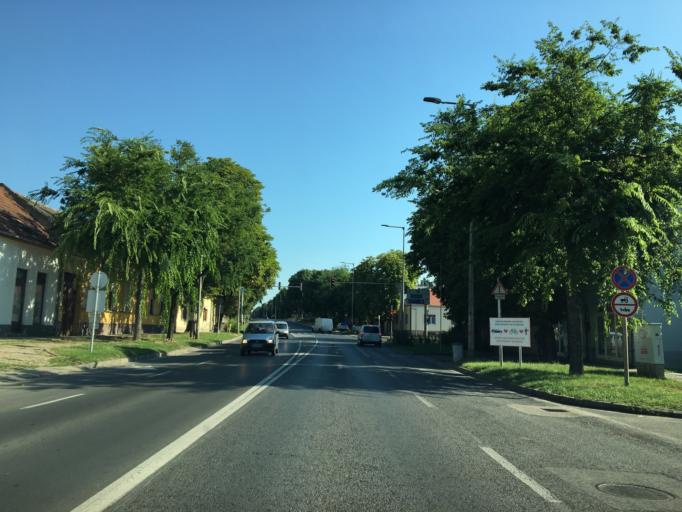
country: HU
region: Tolna
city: Szekszard
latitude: 46.3552
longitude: 18.7038
